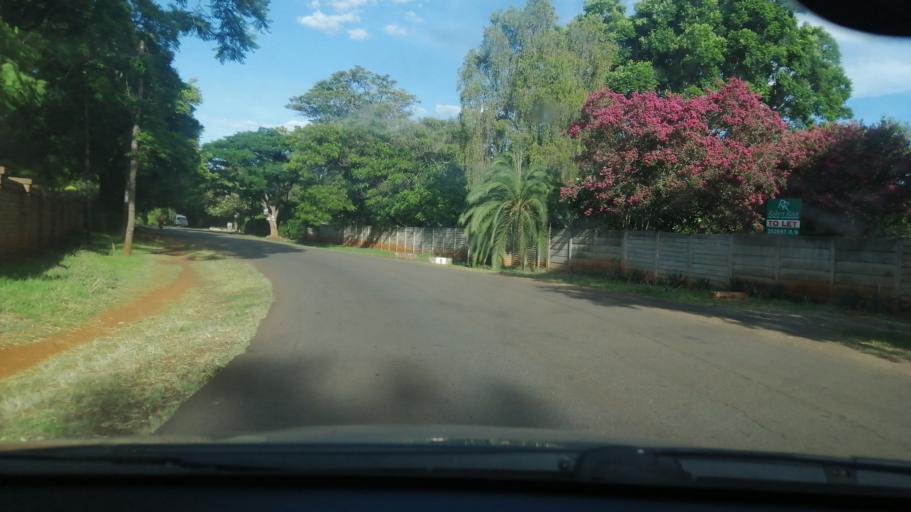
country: ZW
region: Harare
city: Harare
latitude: -17.7659
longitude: 31.0578
